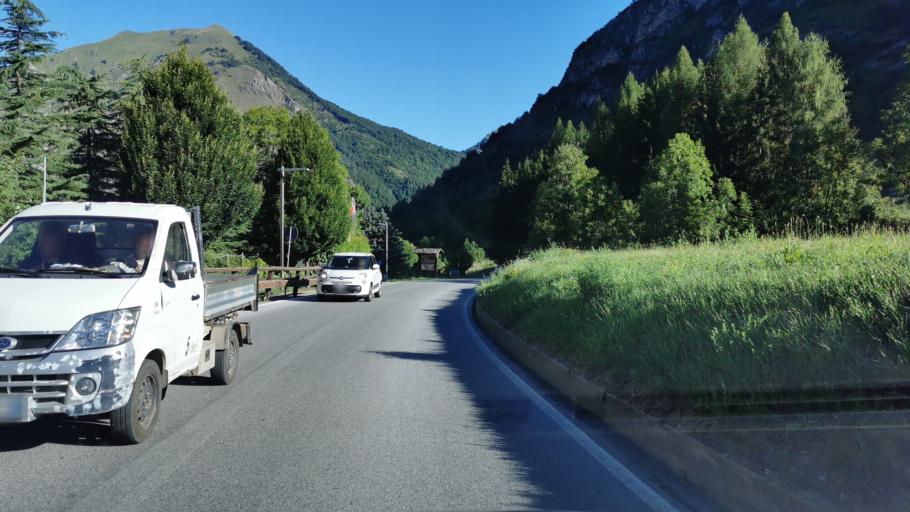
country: IT
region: Piedmont
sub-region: Provincia di Cuneo
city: Entracque
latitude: 44.2503
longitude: 7.3904
